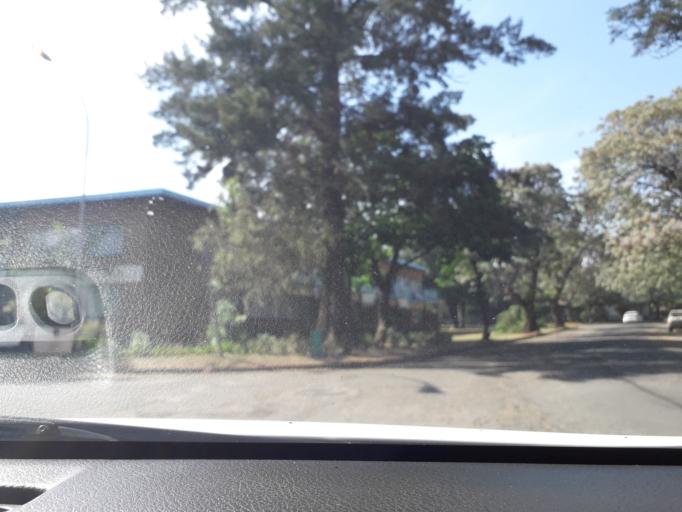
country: ZA
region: Gauteng
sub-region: City of Johannesburg Metropolitan Municipality
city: Modderfontein
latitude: -26.0920
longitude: 28.2372
